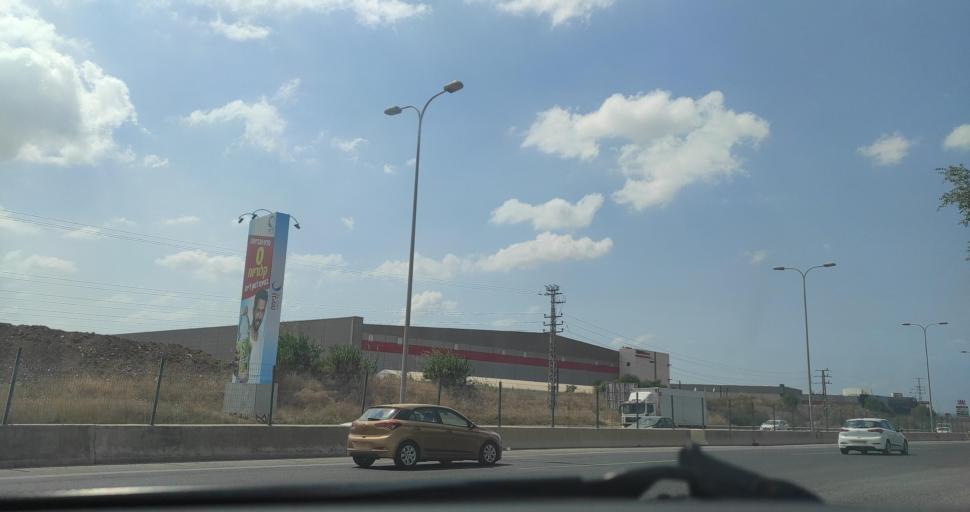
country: IL
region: Central District
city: Rosh Ha'Ayin
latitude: 32.1122
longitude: 34.9546
